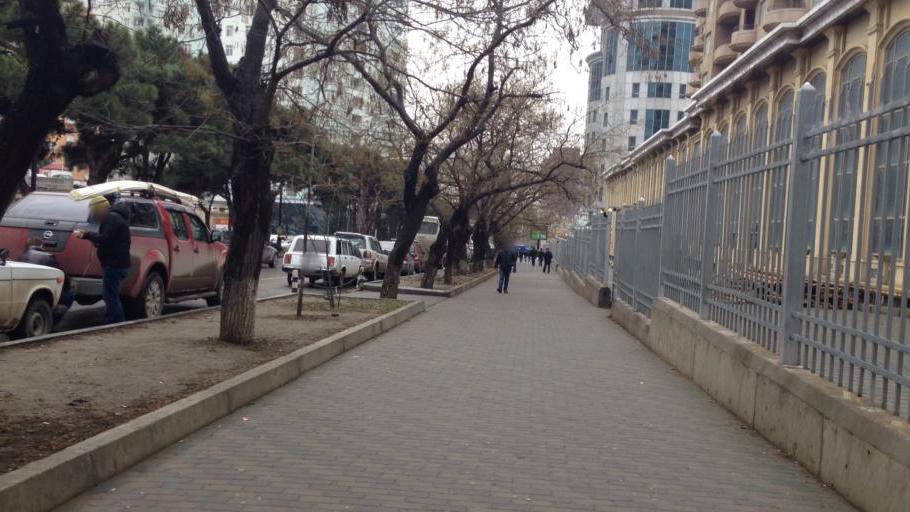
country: AZ
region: Baki
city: Baku
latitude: 40.3835
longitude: 49.8379
